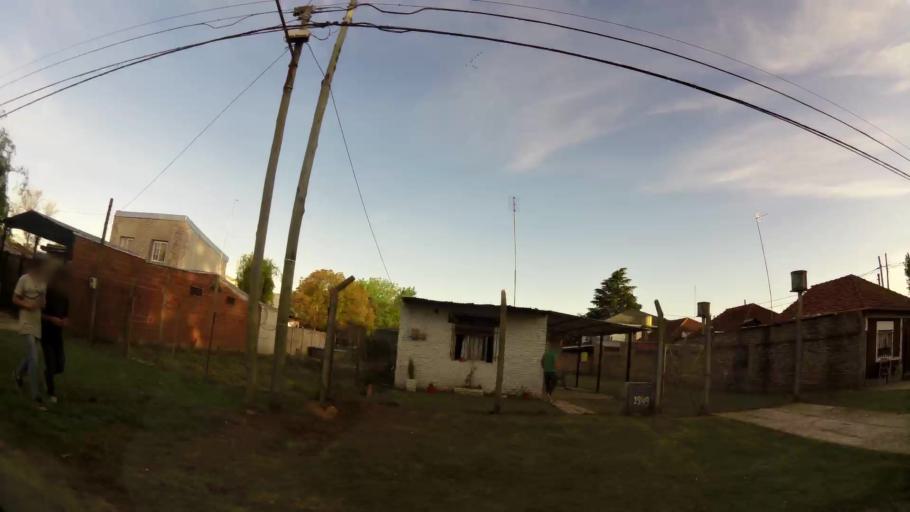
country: AR
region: Buenos Aires
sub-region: Partido de Quilmes
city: Quilmes
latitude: -34.7866
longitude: -58.1875
